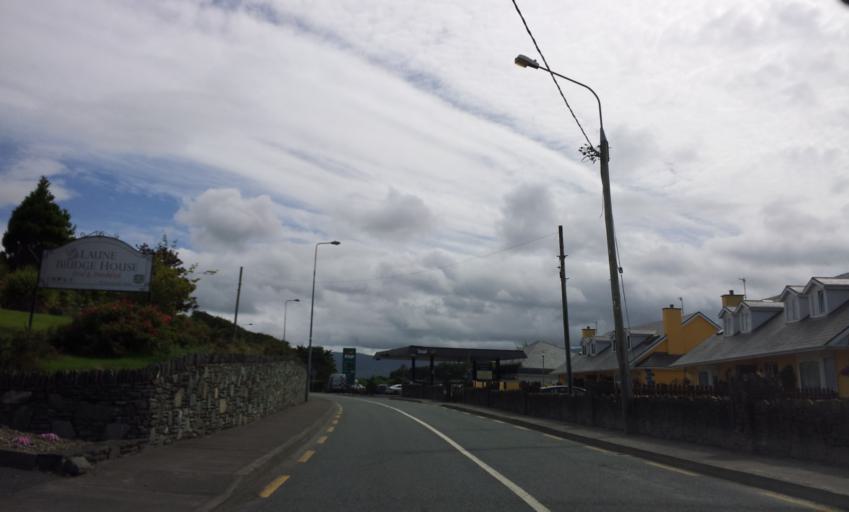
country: IE
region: Munster
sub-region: Ciarrai
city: Killorglin
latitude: 52.1062
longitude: -9.7814
